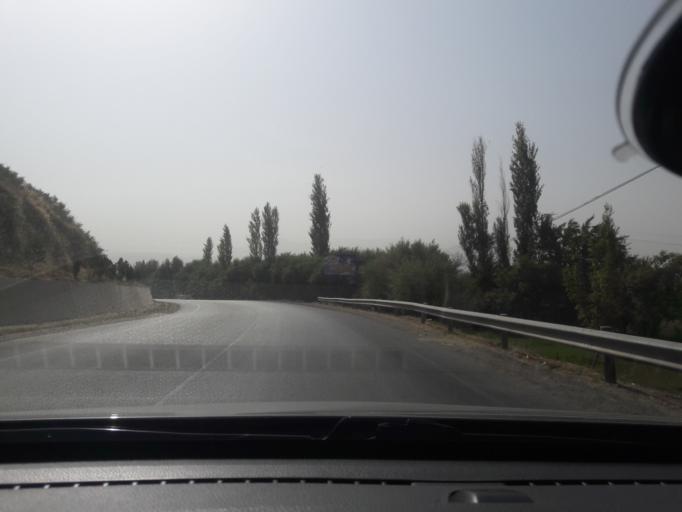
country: TJ
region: Republican Subordination
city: Vahdat
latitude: 38.5206
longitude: 69.0288
